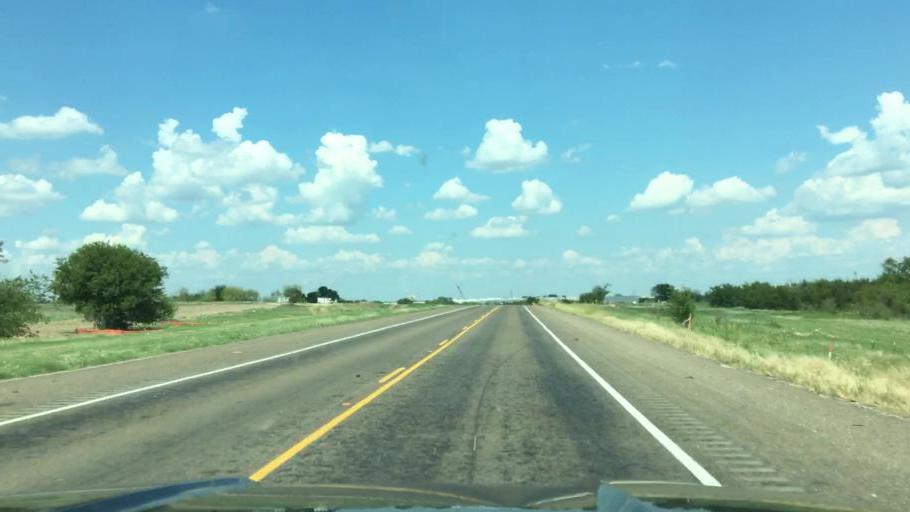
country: US
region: Texas
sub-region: Tarrant County
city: Haslet
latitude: 33.0136
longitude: -97.3360
